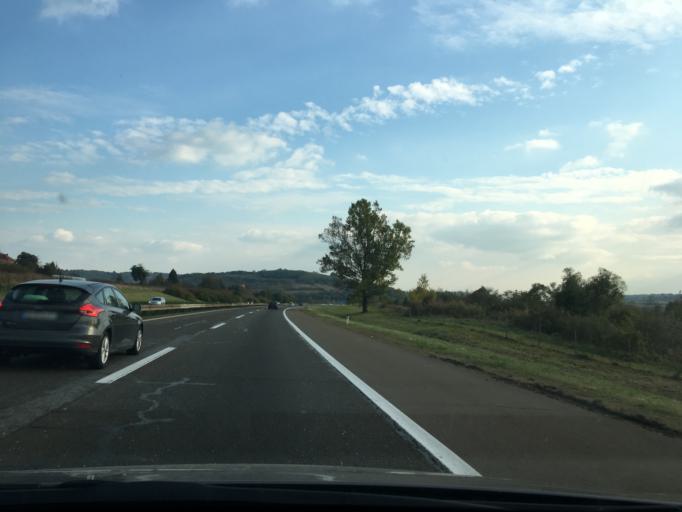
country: RS
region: Central Serbia
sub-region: Belgrade
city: Zvezdara
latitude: 44.6992
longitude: 20.5807
